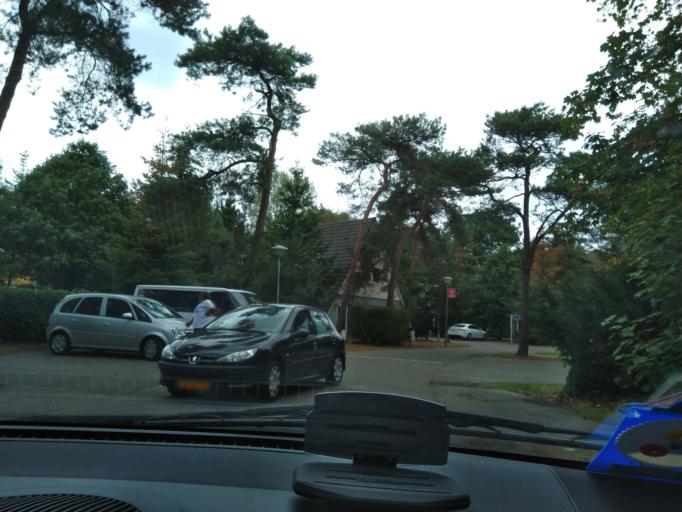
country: NL
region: North Brabant
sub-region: Gemeente Oosterhout
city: Oosterhout
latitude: 51.6321
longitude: 4.8305
